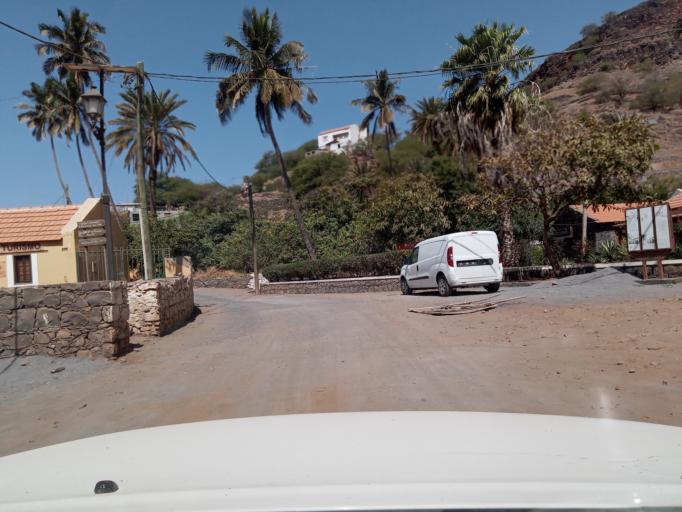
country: CV
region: Ribeira Grande de Santiago
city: Cidade Velha
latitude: 14.9153
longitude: -23.6053
